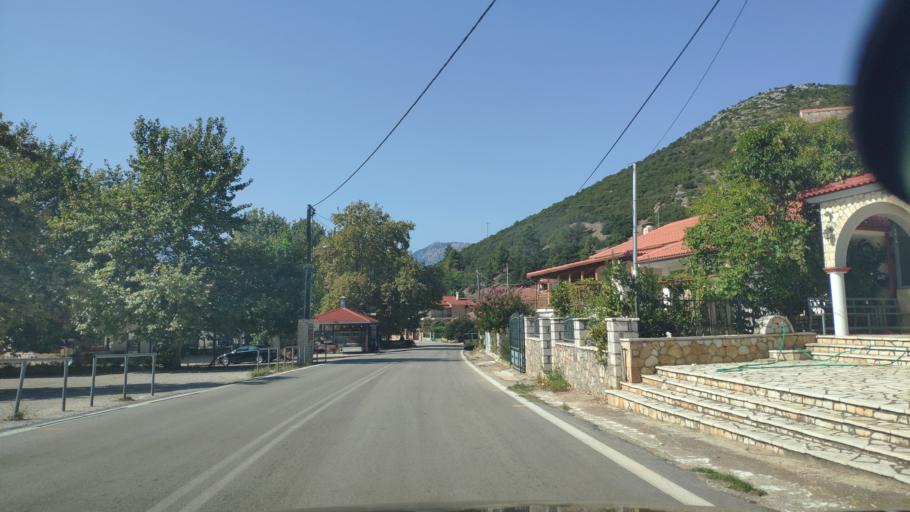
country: GR
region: Peloponnese
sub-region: Nomos Korinthias
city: Nemea
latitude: 37.8706
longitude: 22.4665
